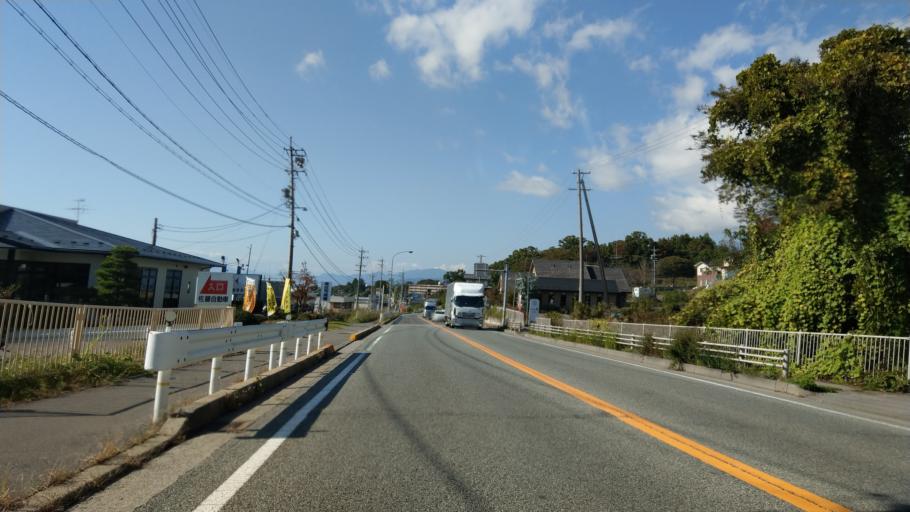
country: JP
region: Nagano
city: Komoro
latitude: 36.3186
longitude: 138.4403
